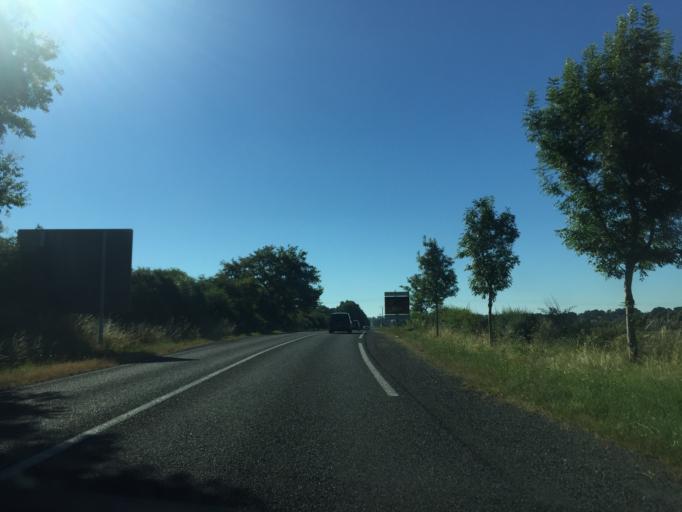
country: FR
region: Auvergne
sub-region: Departement de l'Allier
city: Dompierre-sur-Besbre
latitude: 46.5367
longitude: 3.6565
